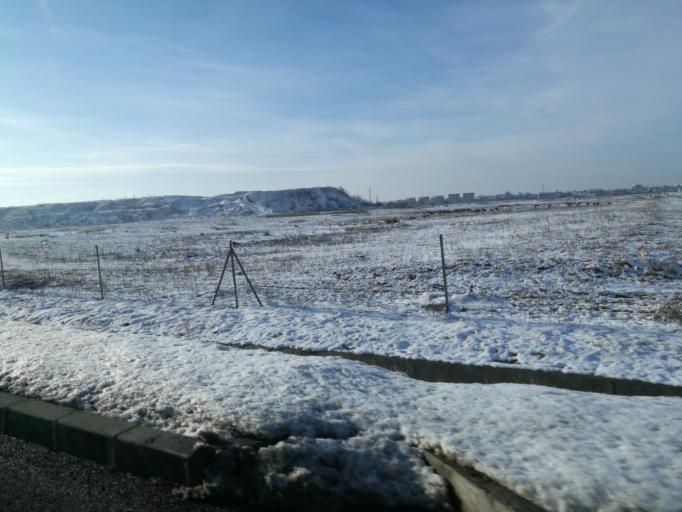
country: RO
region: Ilfov
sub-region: Voluntari City
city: Voluntari
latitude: 44.5008
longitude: 26.1544
